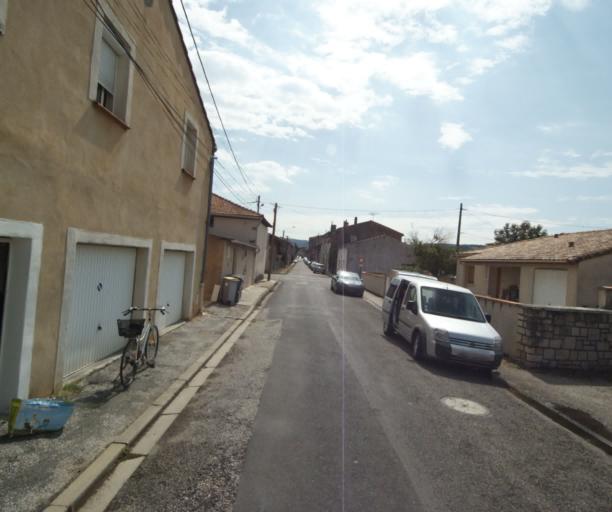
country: FR
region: Midi-Pyrenees
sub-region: Departement de la Haute-Garonne
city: Revel
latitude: 43.4602
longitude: 1.9991
